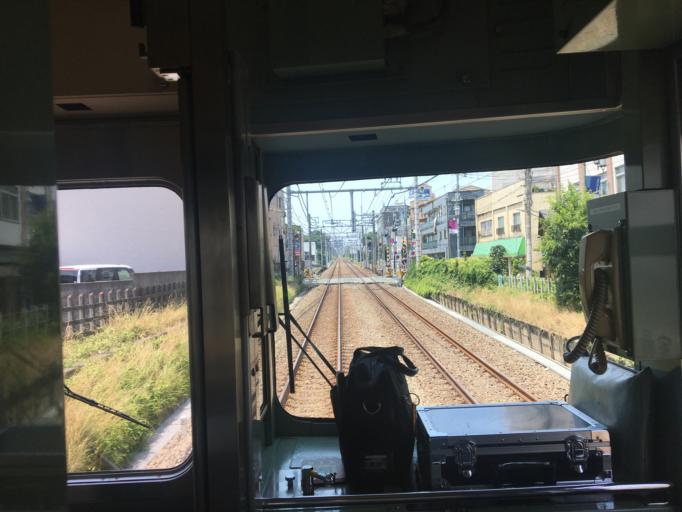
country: JP
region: Tokyo
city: Tanashicho
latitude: 35.7617
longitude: 139.5326
